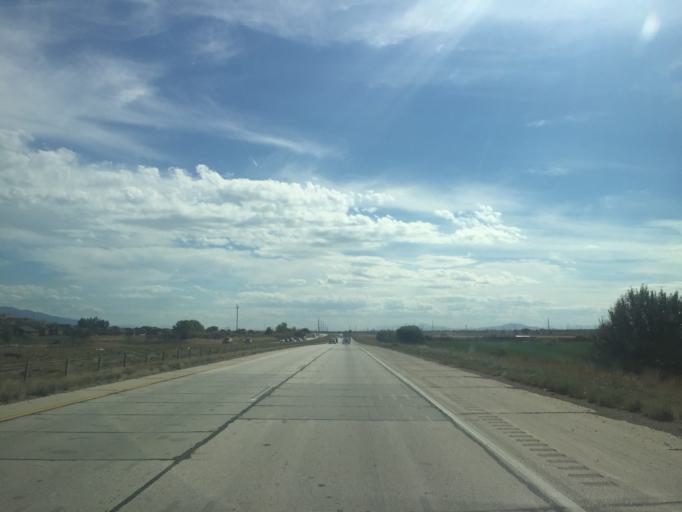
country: US
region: Utah
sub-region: Box Elder County
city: South Willard
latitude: 41.3679
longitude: -112.0431
